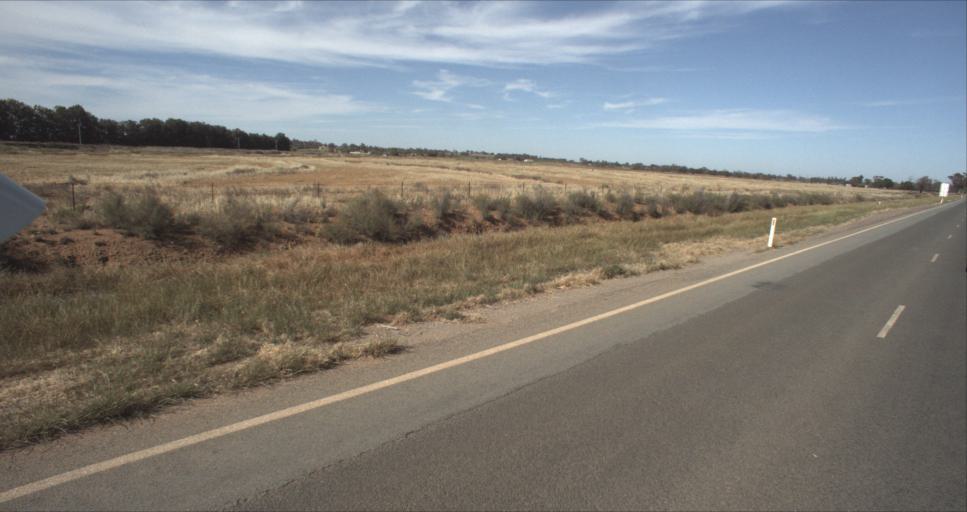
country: AU
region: New South Wales
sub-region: Leeton
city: Leeton
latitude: -34.5567
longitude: 146.4486
